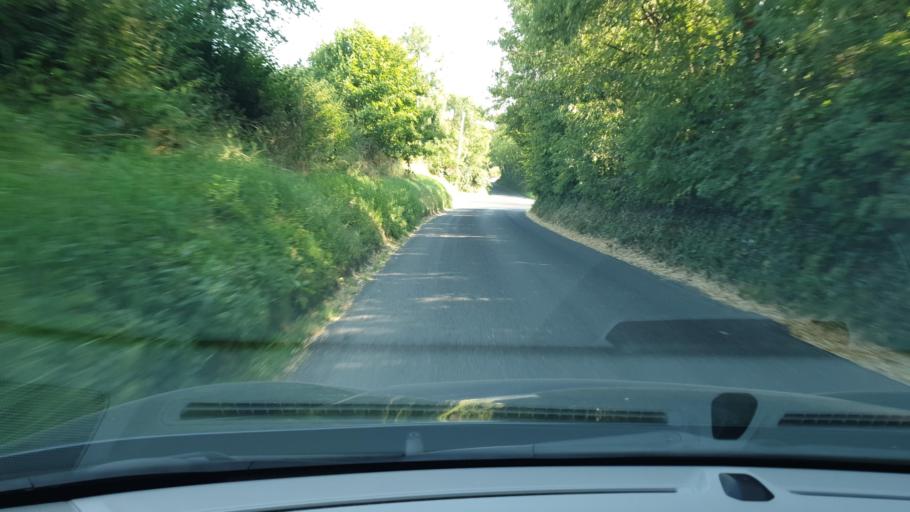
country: IE
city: Kentstown
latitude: 53.5965
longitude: -6.4902
